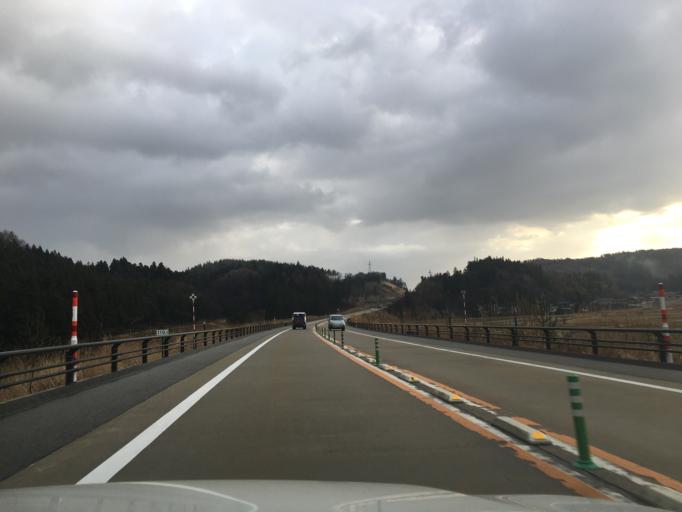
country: JP
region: Yamagata
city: Tsuruoka
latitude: 38.6953
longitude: 139.6953
